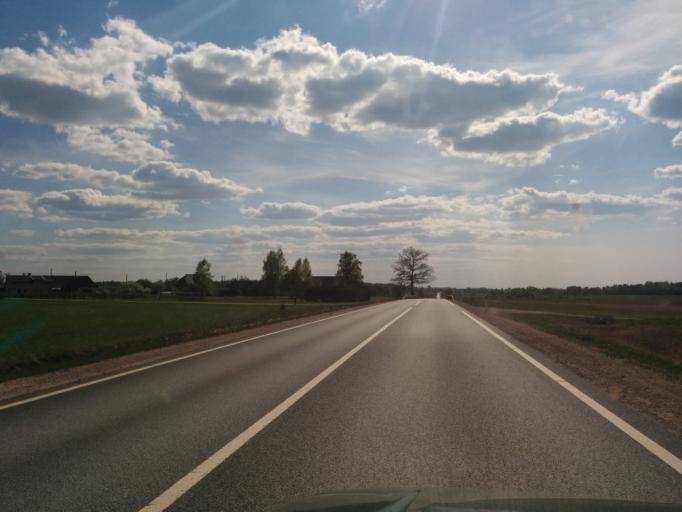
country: LV
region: Sigulda
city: Sigulda
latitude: 57.2586
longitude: 24.8675
